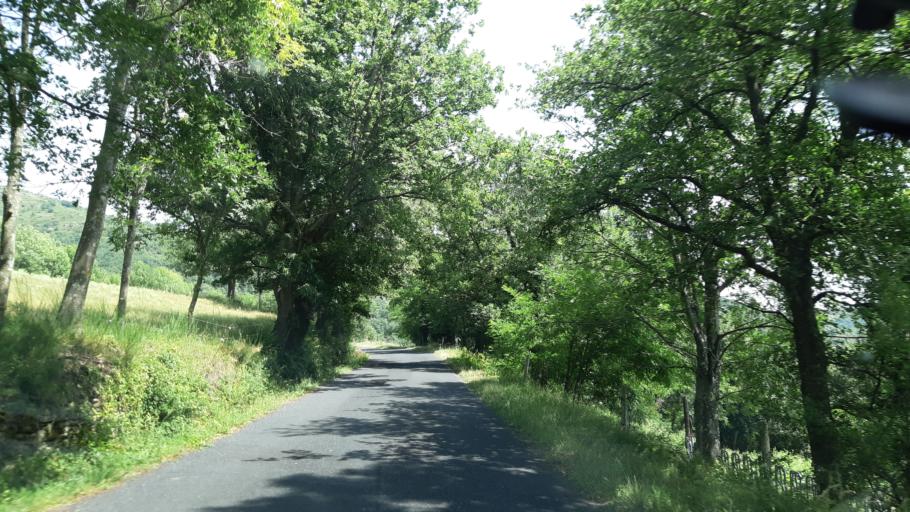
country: FR
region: Languedoc-Roussillon
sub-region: Departement des Pyrenees-Orientales
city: Arles
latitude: 42.5272
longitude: 2.6147
